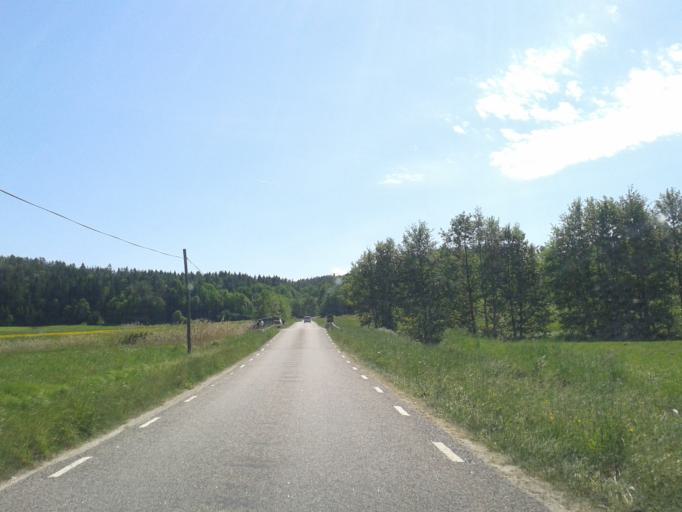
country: SE
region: Vaestra Goetaland
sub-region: Stenungsunds Kommun
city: Stora Hoga
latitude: 58.0165
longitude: 11.9262
